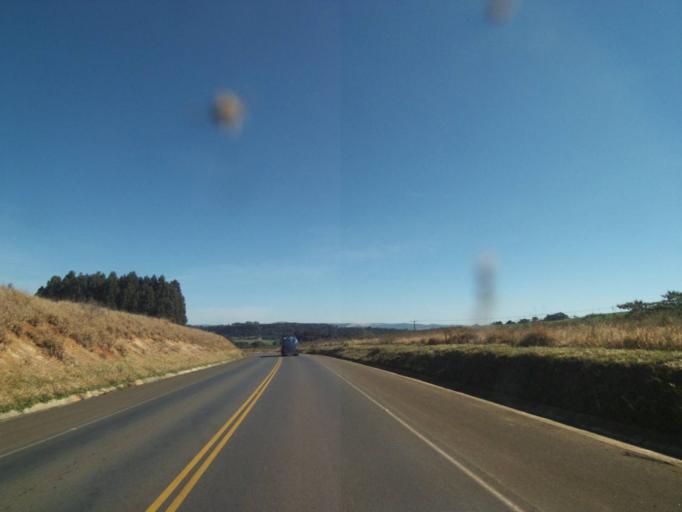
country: BR
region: Parana
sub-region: Tibagi
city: Tibagi
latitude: -24.4648
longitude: -50.4374
